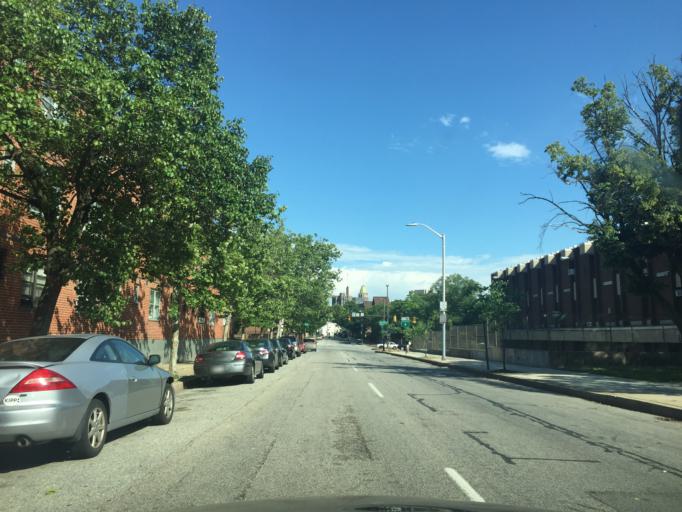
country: US
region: Maryland
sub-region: City of Baltimore
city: Baltimore
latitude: 39.2992
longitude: -76.6251
